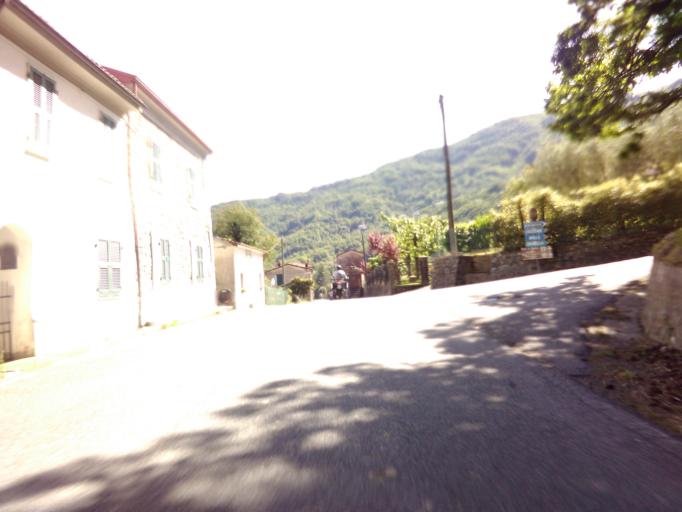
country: IT
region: Tuscany
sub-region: Provincia di Massa-Carrara
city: Comano
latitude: 44.3037
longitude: 10.0769
